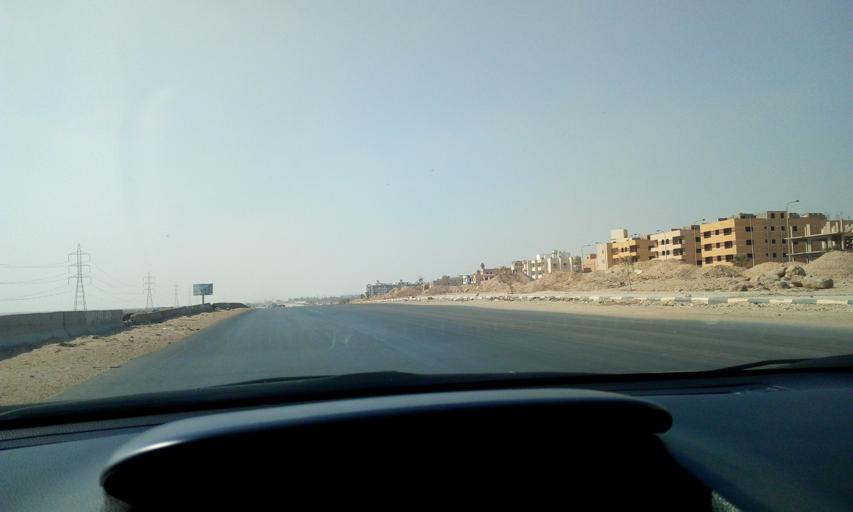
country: EG
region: Al Jizah
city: Madinat Sittah Uktubar
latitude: 29.8978
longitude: 31.0846
